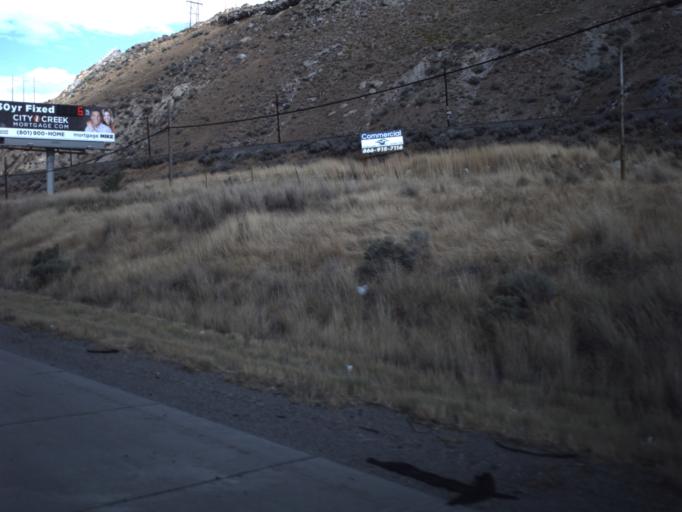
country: US
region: Utah
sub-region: Tooele County
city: Stansbury park
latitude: 40.7028
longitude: -112.2568
